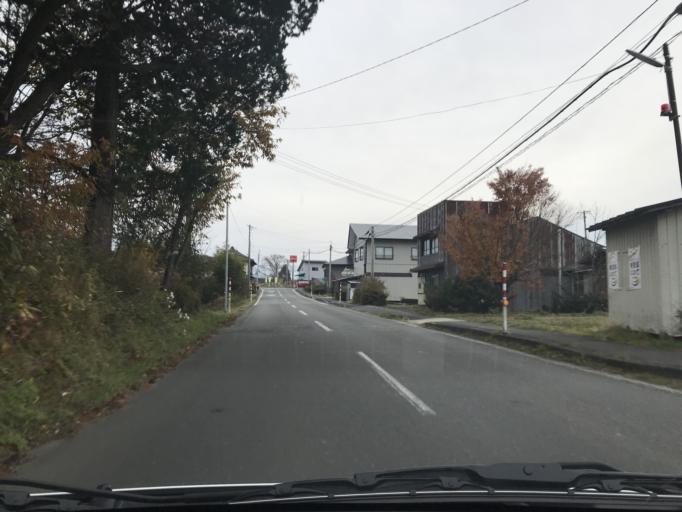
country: JP
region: Iwate
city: Kitakami
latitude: 39.2783
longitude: 141.2656
